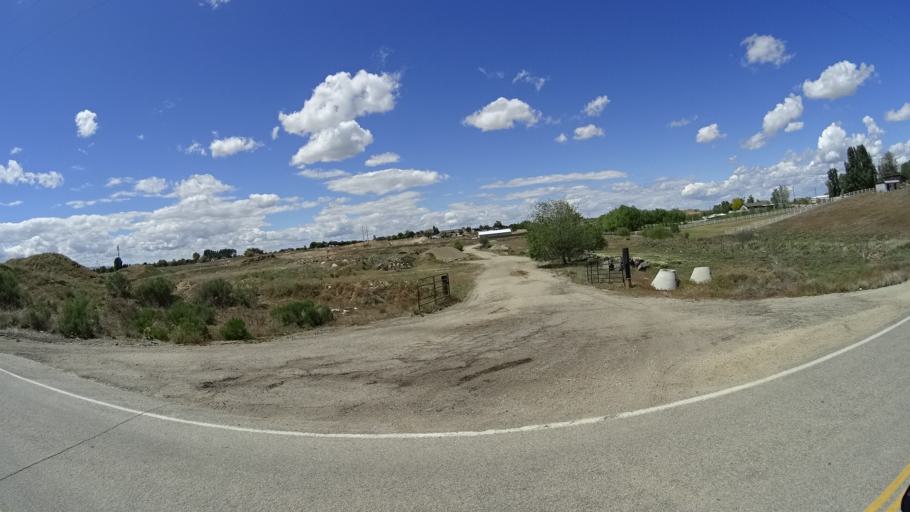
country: US
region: Idaho
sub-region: Ada County
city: Meridian
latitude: 43.5848
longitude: -116.4736
